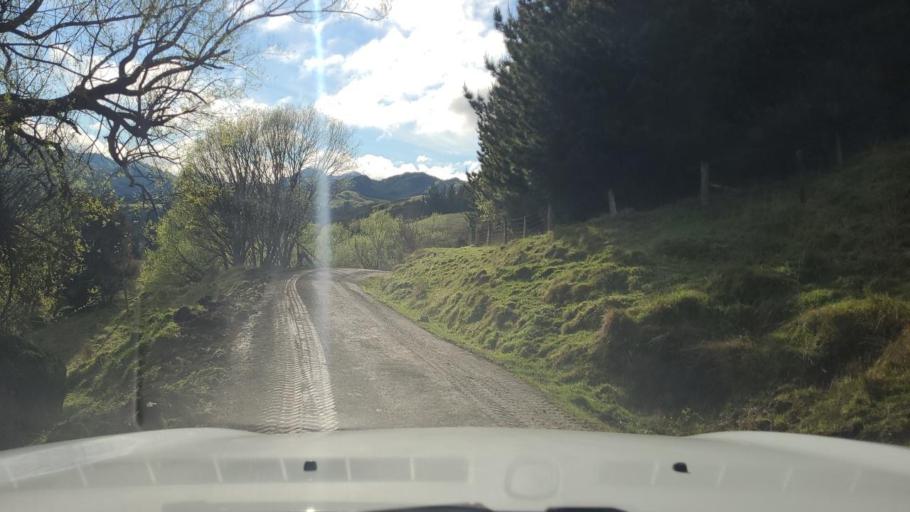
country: NZ
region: Wellington
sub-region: South Wairarapa District
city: Waipawa
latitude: -41.2398
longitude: 175.6964
